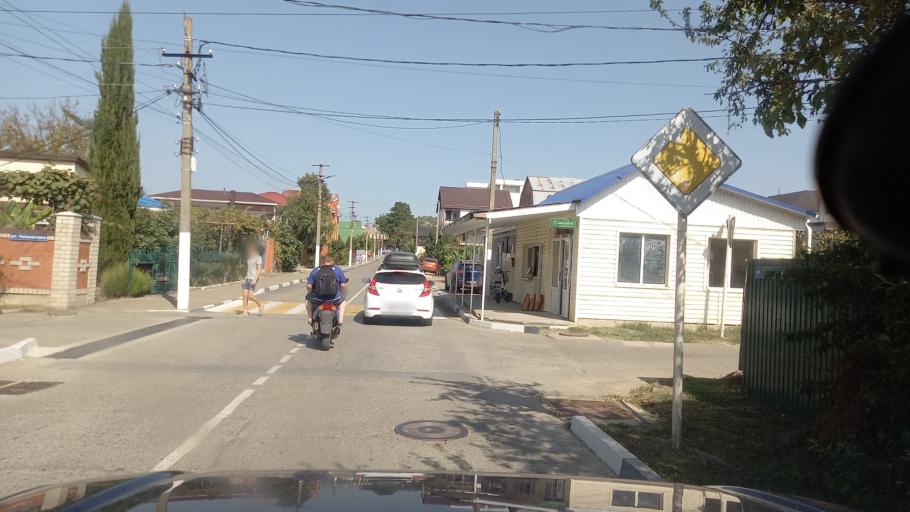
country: RU
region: Krasnodarskiy
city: Arkhipo-Osipovka
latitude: 44.3682
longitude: 38.5321
